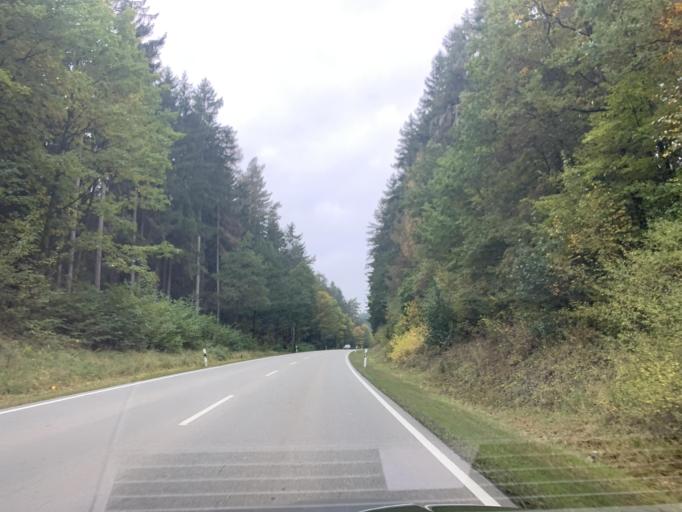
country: DE
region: Bavaria
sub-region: Upper Palatinate
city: Teunz
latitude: 49.4776
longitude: 12.3689
